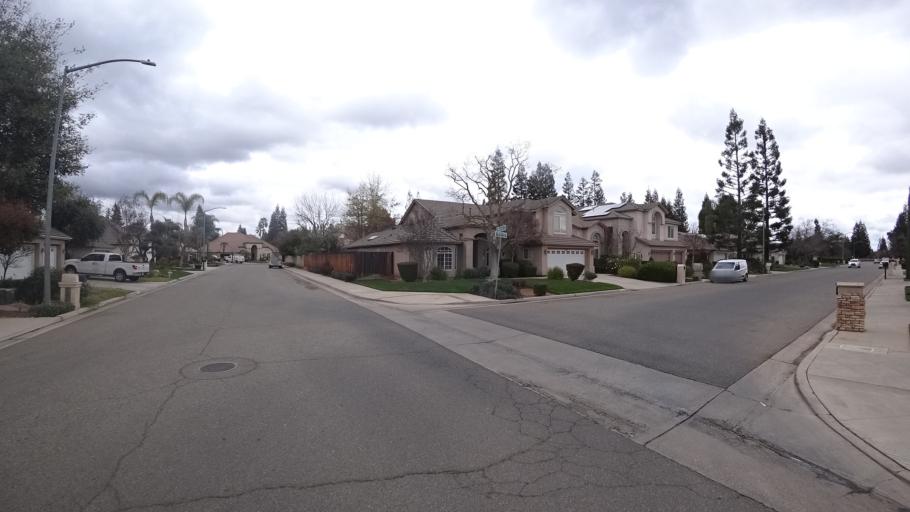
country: US
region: California
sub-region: Fresno County
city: Fresno
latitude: 36.8395
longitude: -119.8293
